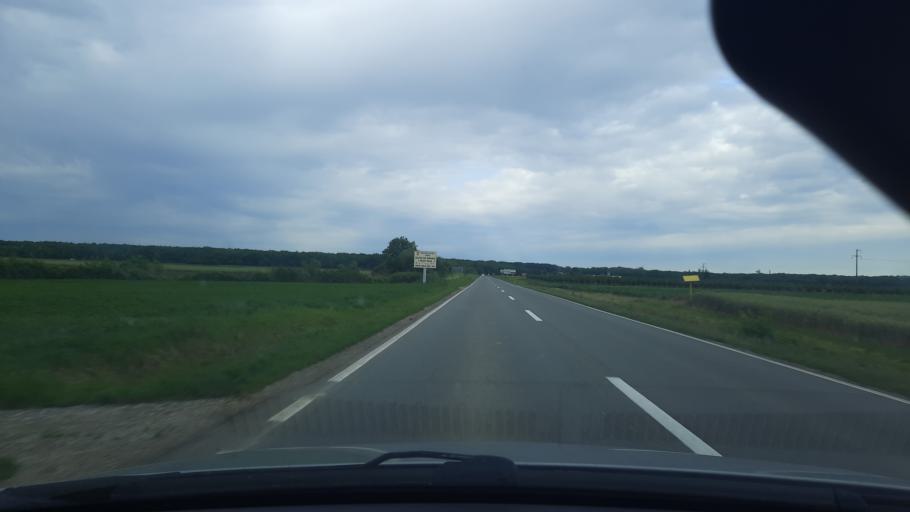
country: RS
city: Platicevo
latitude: 44.8139
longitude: 19.7674
